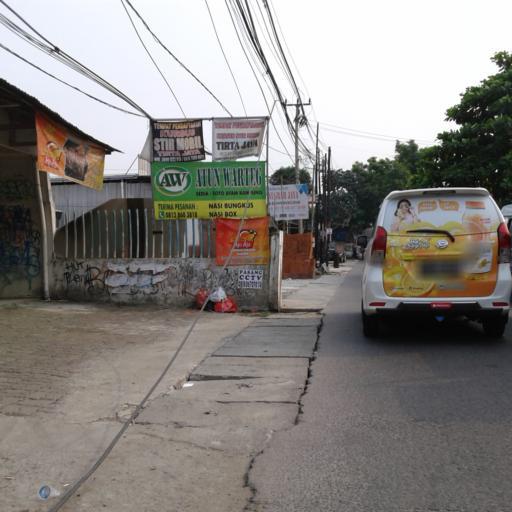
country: ID
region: West Java
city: Sawangan
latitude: -6.3709
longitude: 106.7734
